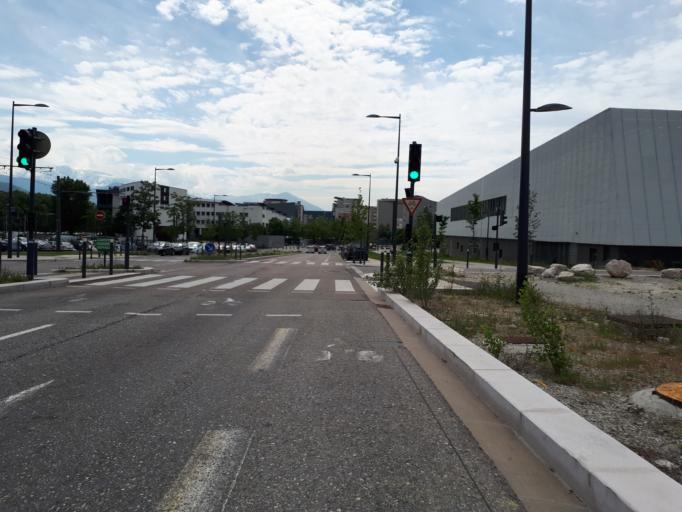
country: FR
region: Rhone-Alpes
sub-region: Departement de l'Isere
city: Saint-Martin-le-Vinoux
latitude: 45.1967
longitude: 5.7102
